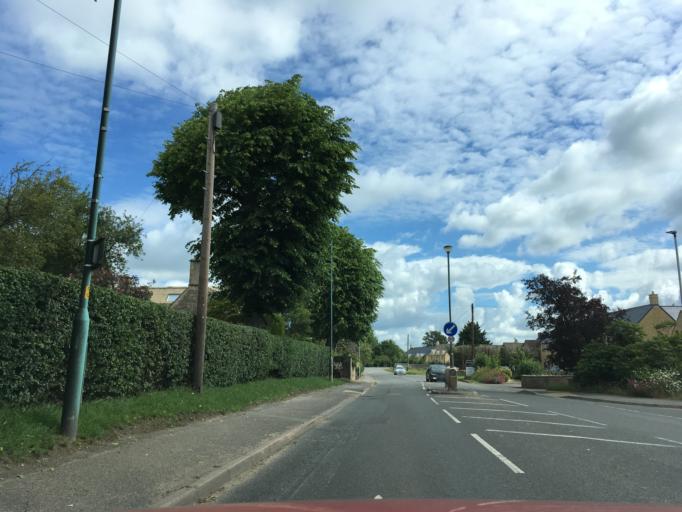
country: GB
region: England
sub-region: Gloucestershire
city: Lechlade
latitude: 51.7016
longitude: -1.6878
